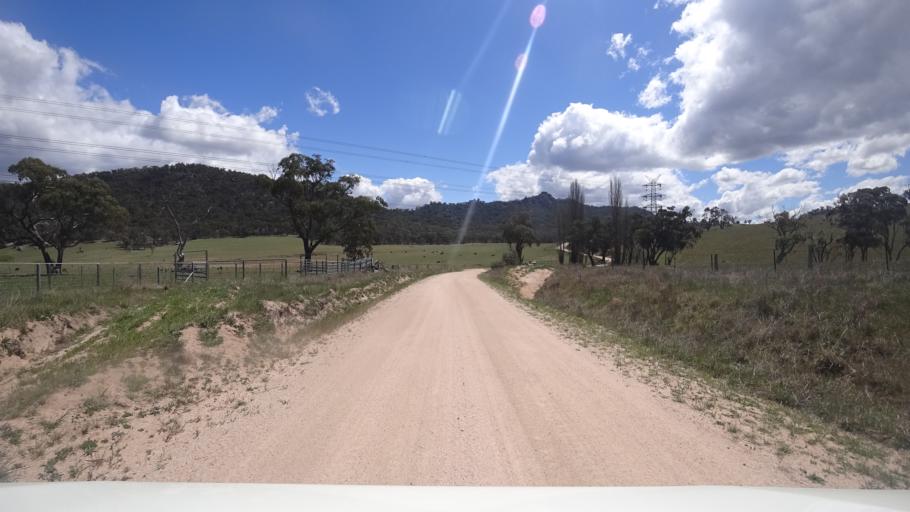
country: AU
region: New South Wales
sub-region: Oberon
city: Oberon
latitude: -33.5592
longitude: 149.9345
